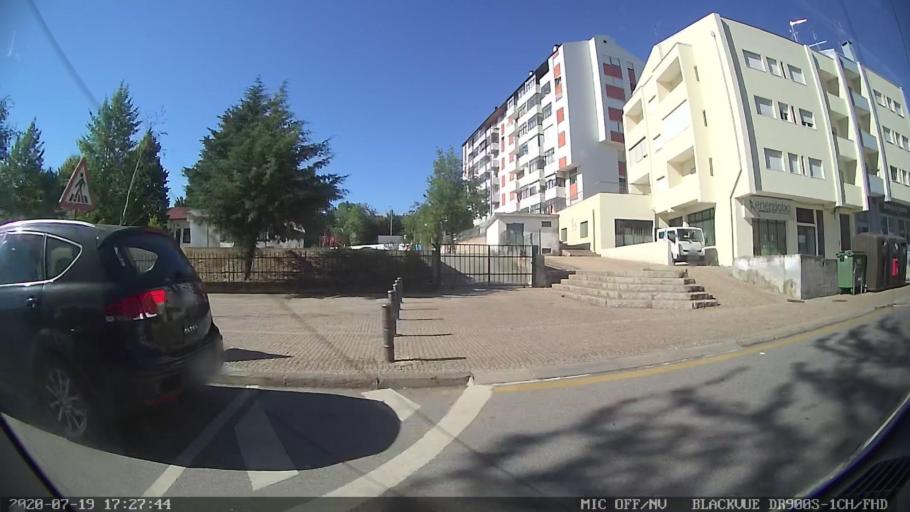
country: PT
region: Braganca
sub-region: Braganca Municipality
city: Braganca
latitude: 41.7998
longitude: -6.7683
